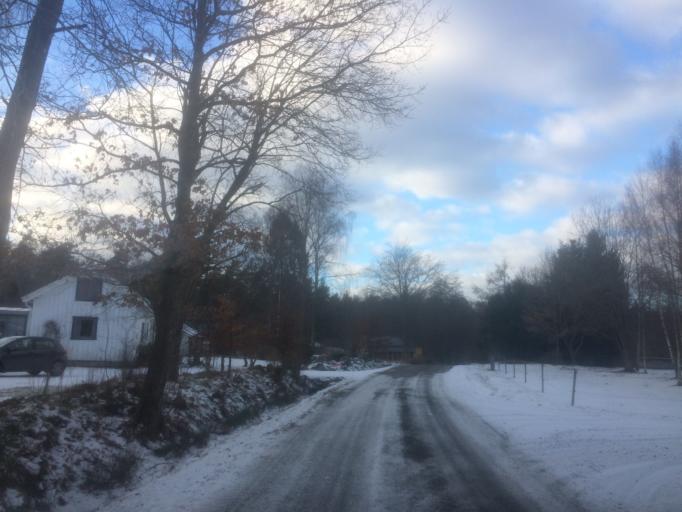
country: SE
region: Vaestra Goetaland
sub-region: Kungalvs Kommun
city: Kungalv
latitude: 57.8289
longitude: 11.9719
